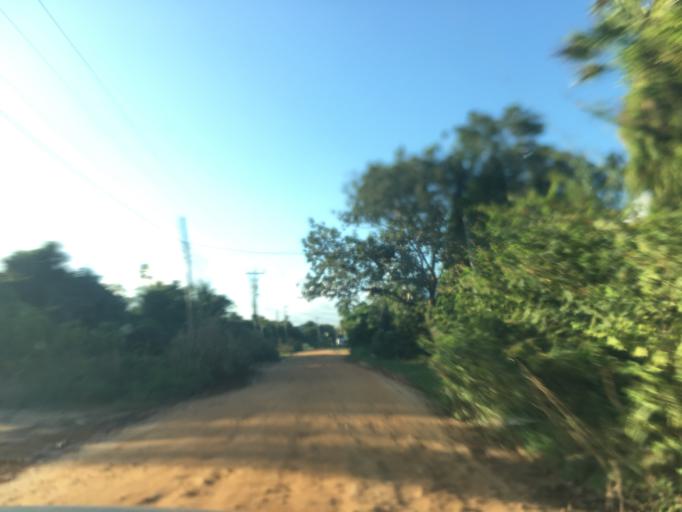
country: BZ
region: Stann Creek
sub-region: Dangriga
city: Dangriga
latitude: 16.8368
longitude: -88.2683
